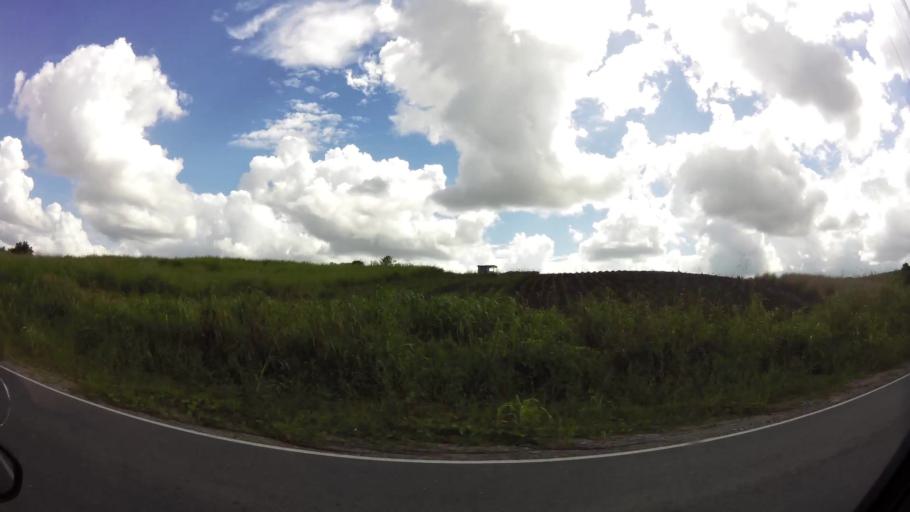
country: TT
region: Penal/Debe
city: Debe
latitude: 10.2313
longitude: -61.4825
